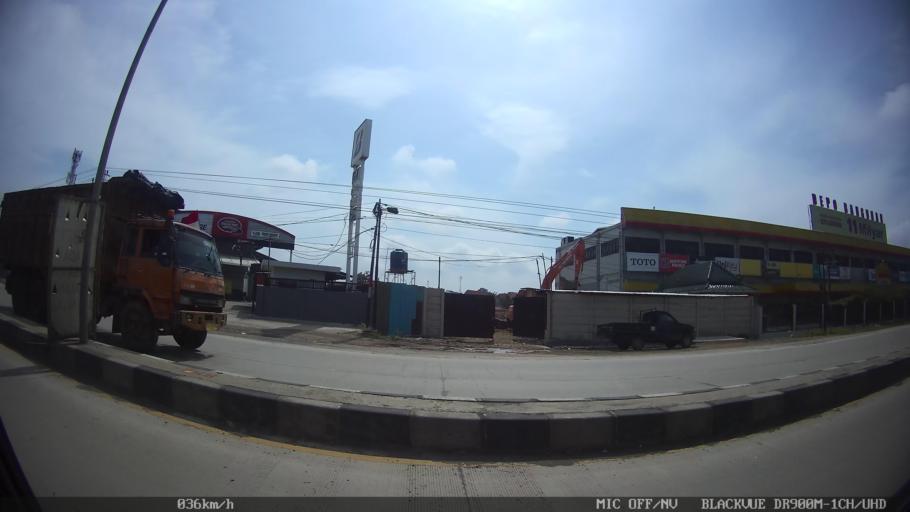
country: ID
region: Lampung
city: Kedaton
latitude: -5.3919
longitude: 105.2886
